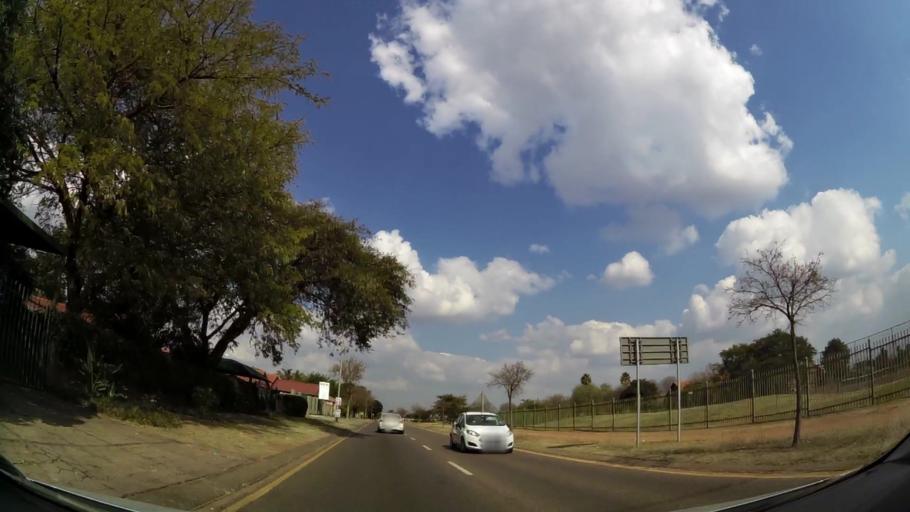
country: ZA
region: Gauteng
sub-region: City of Tshwane Metropolitan Municipality
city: Centurion
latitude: -25.8429
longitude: 28.2445
